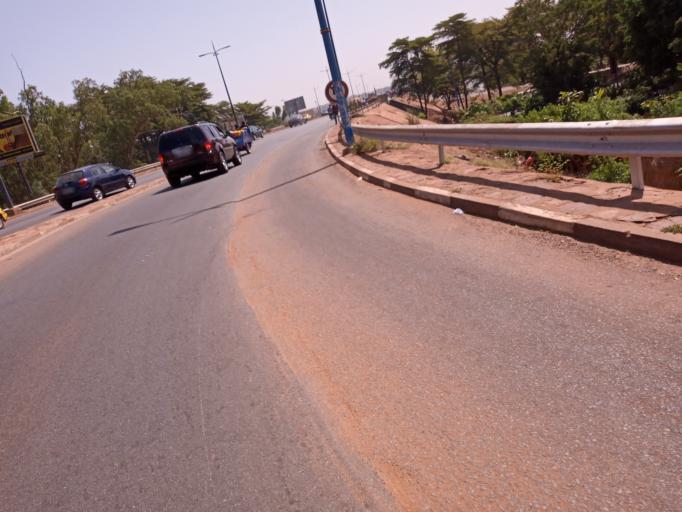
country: ML
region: Bamako
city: Bamako
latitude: 12.6284
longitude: -8.0086
